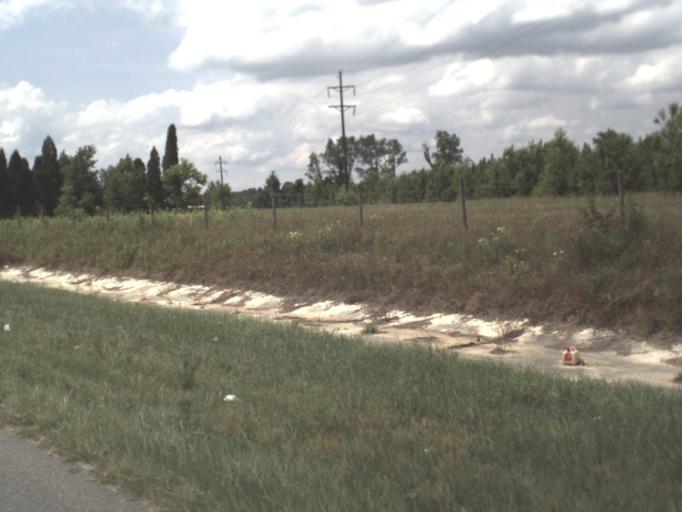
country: US
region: Florida
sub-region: Hamilton County
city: Jasper
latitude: 30.4944
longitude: -82.9318
